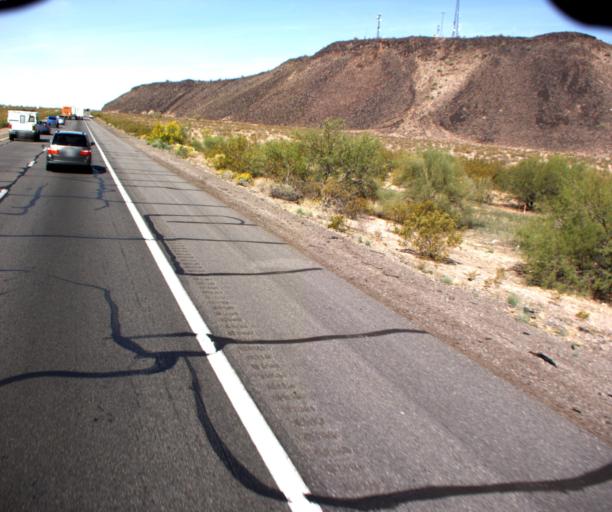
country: US
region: Arizona
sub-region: Maricopa County
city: Buckeye
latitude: 33.5264
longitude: -113.1020
